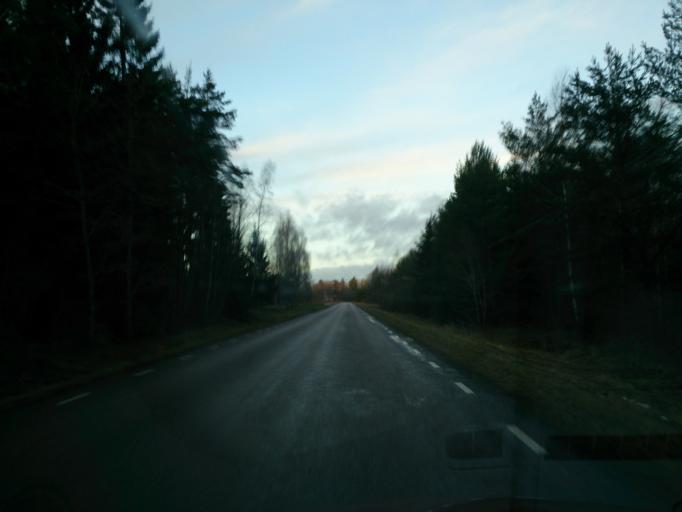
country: SE
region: OEstergoetland
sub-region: Atvidabergs Kommun
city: Atvidaberg
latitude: 58.3230
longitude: 16.0265
